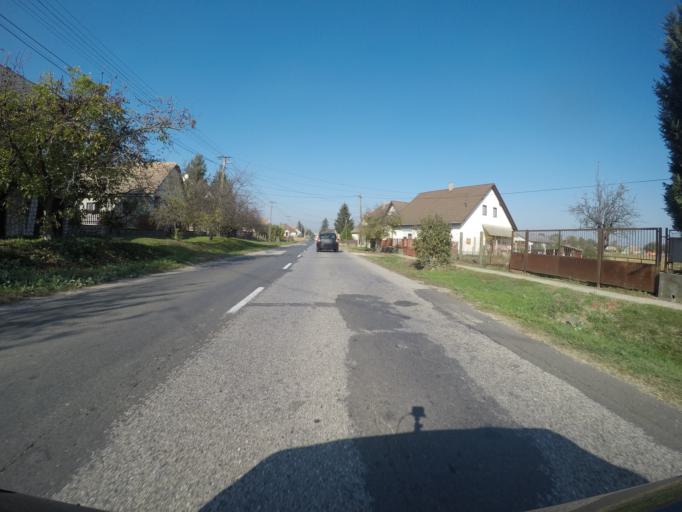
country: HU
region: Tolna
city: Szedres
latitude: 46.4815
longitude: 18.6830
